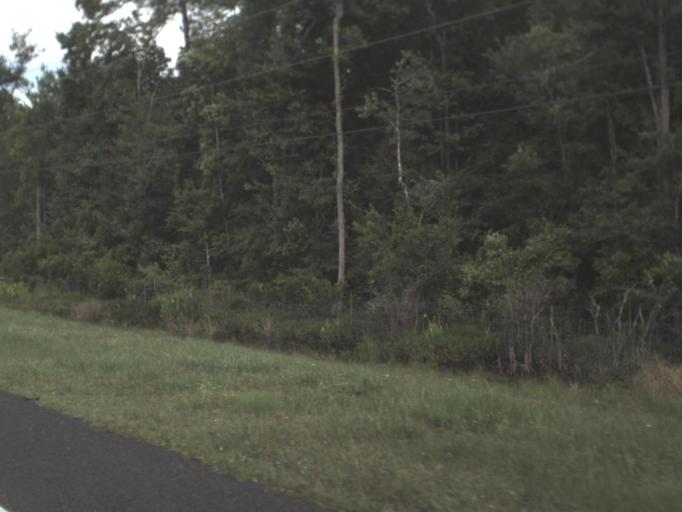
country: US
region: Florida
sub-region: Nassau County
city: Callahan
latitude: 30.6120
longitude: -81.7322
